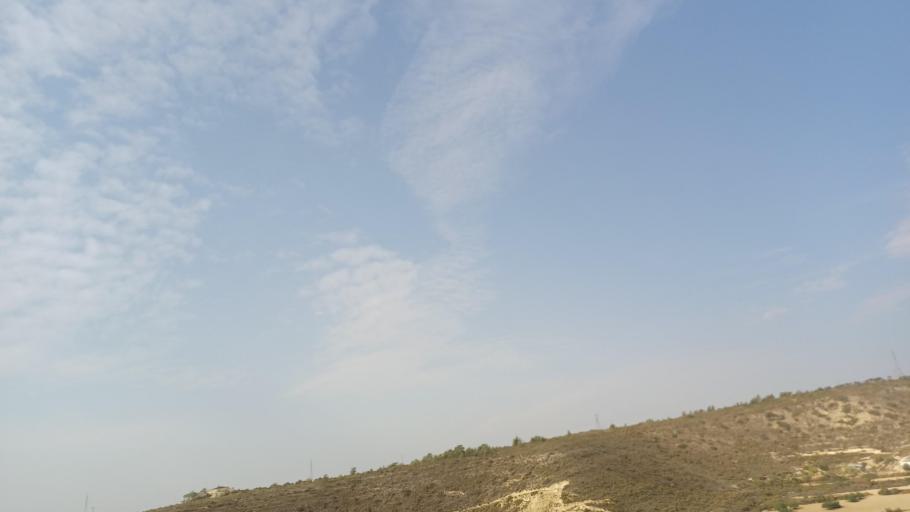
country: CY
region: Limassol
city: Ypsonas
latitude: 34.7441
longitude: 32.9482
